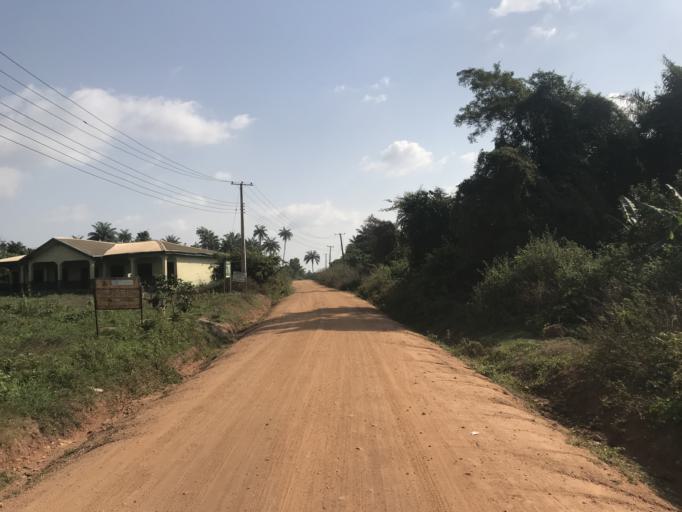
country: NG
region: Osun
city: Ikirun
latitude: 7.8621
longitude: 4.5881
